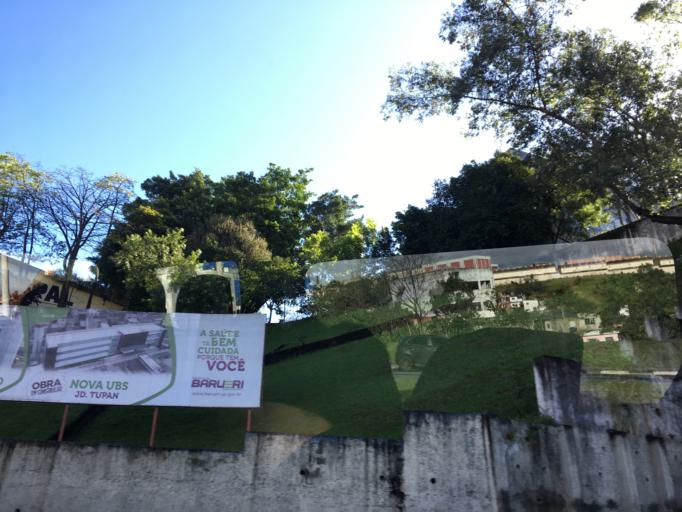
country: BR
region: Sao Paulo
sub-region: Barueri
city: Barueri
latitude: -23.4929
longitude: -46.8795
